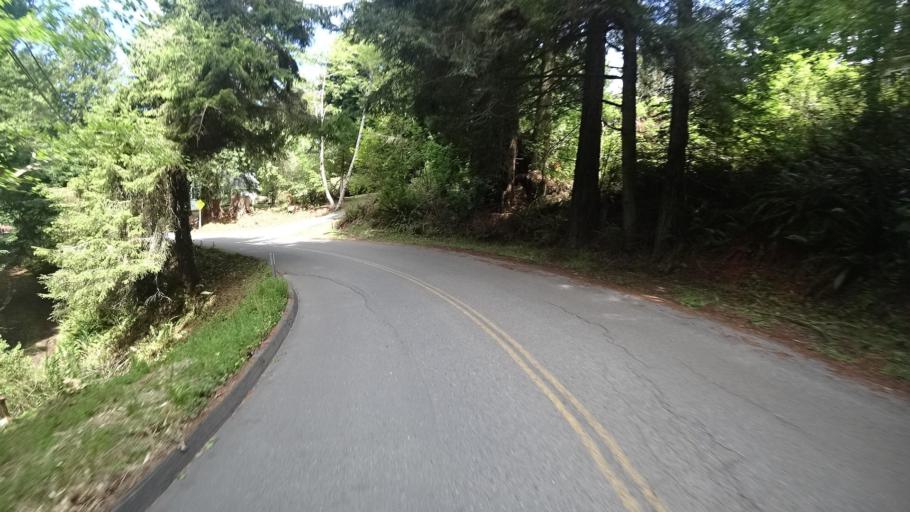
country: US
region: California
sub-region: Humboldt County
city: Arcata
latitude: 40.8700
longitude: -124.0588
